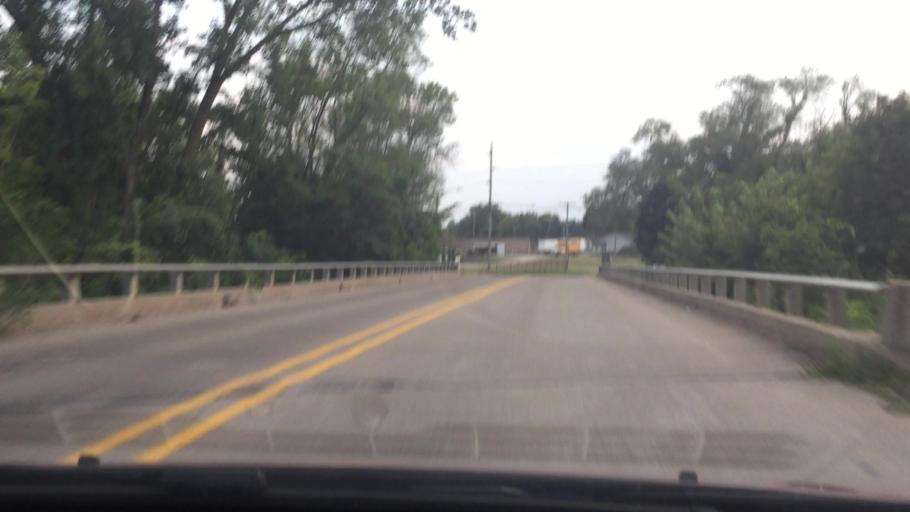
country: US
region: Iowa
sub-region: Muscatine County
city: Muscatine
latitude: 41.4452
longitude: -91.0396
